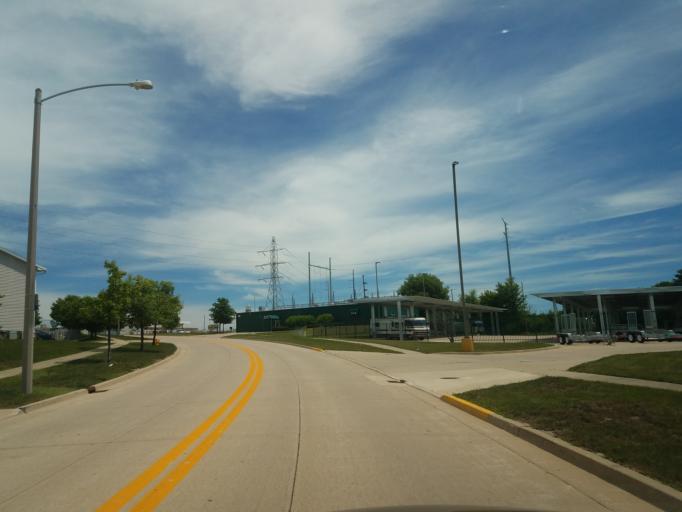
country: US
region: Illinois
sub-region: McLean County
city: Bloomington
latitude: 40.4605
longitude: -88.9894
